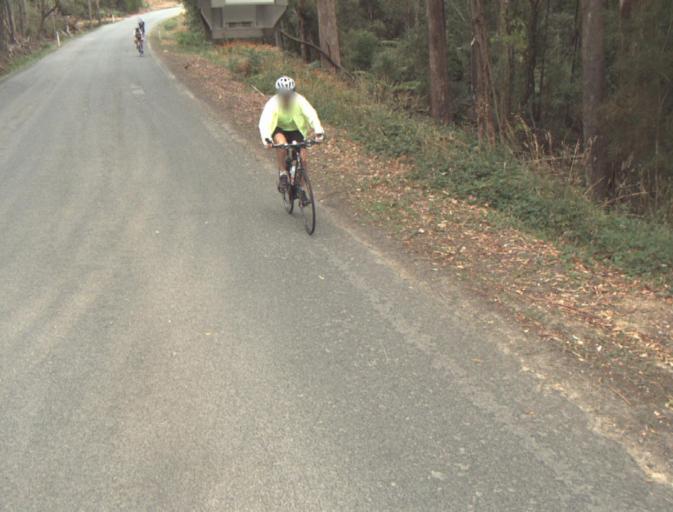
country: AU
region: Tasmania
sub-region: Launceston
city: Mayfield
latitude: -41.2141
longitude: 147.2118
